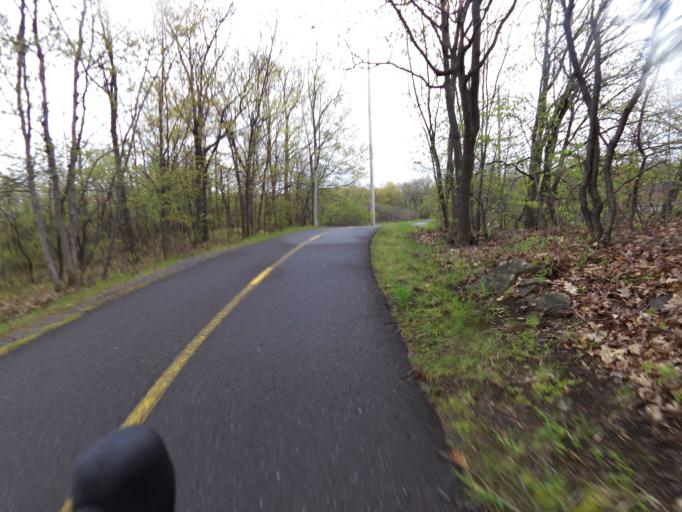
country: CA
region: Ontario
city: Ottawa
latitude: 45.4198
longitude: -75.7388
